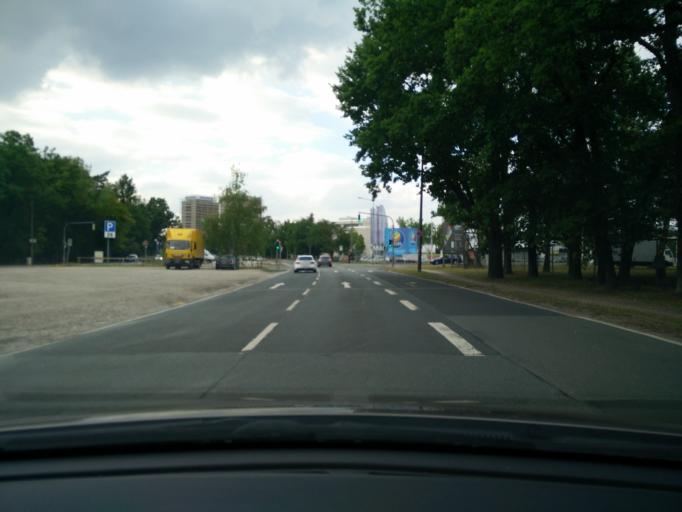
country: DE
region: Bavaria
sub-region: Regierungsbezirk Mittelfranken
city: Nuernberg
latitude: 49.4241
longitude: 11.1335
